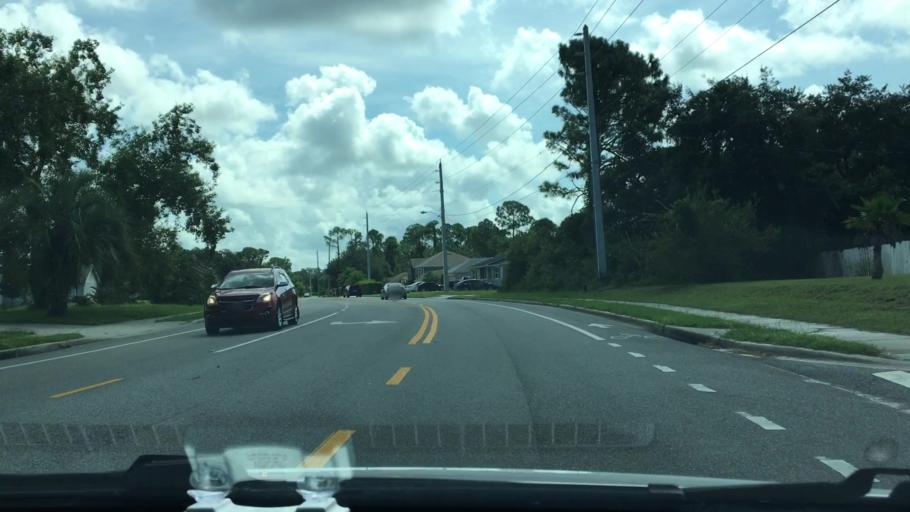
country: US
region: Florida
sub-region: Volusia County
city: Deltona
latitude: 28.8773
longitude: -81.1858
